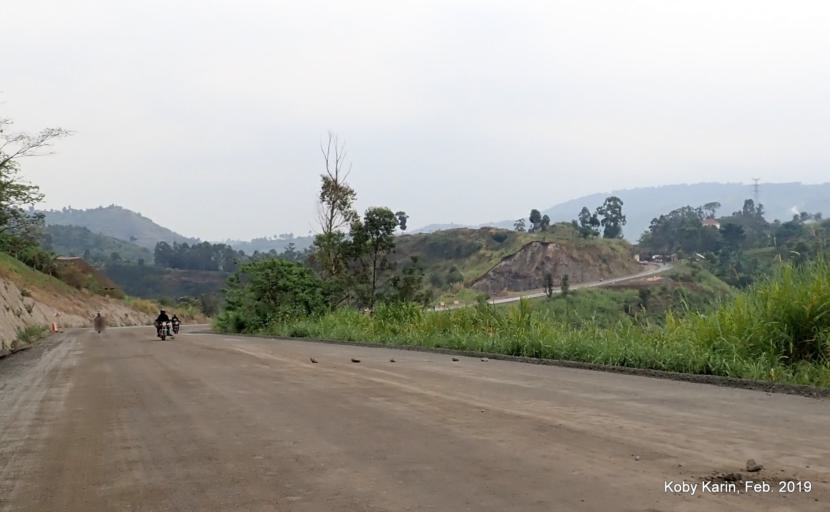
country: UG
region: Western Region
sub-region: Rubirizi District
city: Rubirizi
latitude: -0.2551
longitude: 30.0912
